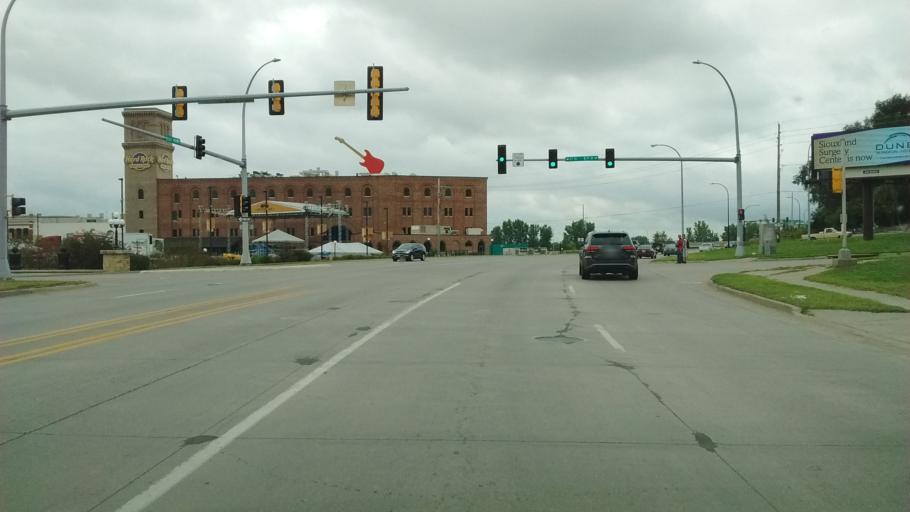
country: US
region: Iowa
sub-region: Woodbury County
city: Sioux City
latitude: 42.4955
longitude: -96.4107
